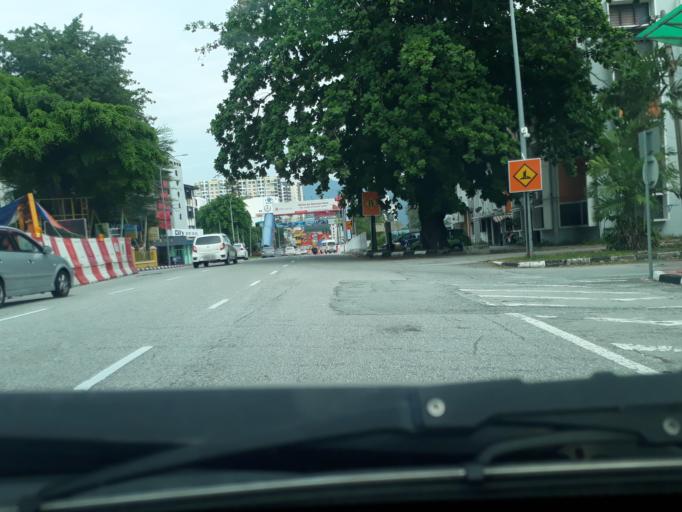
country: MY
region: Perak
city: Ipoh
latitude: 4.5919
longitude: 101.0892
